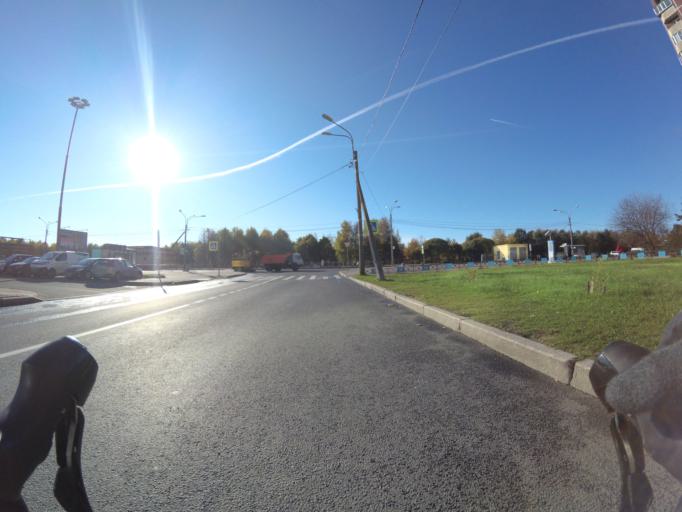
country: RU
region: Leningrad
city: Untolovo
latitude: 59.9852
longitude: 30.2009
